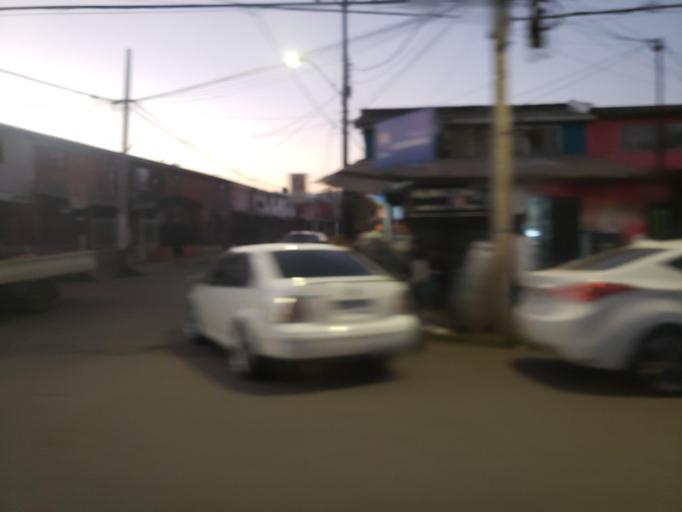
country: CL
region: Santiago Metropolitan
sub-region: Provincia de Talagante
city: El Monte
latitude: -33.6841
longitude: -71.0014
